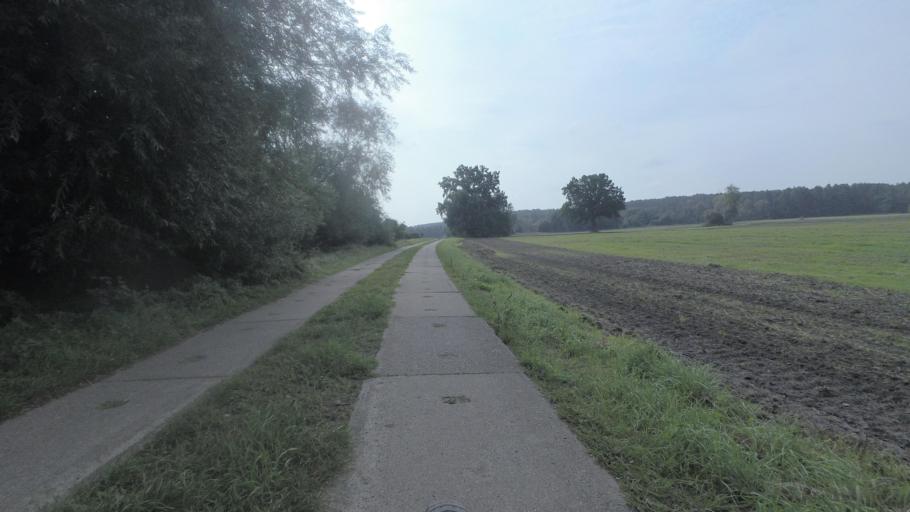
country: DE
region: Brandenburg
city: Rangsdorf
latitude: 52.2737
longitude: 13.3896
